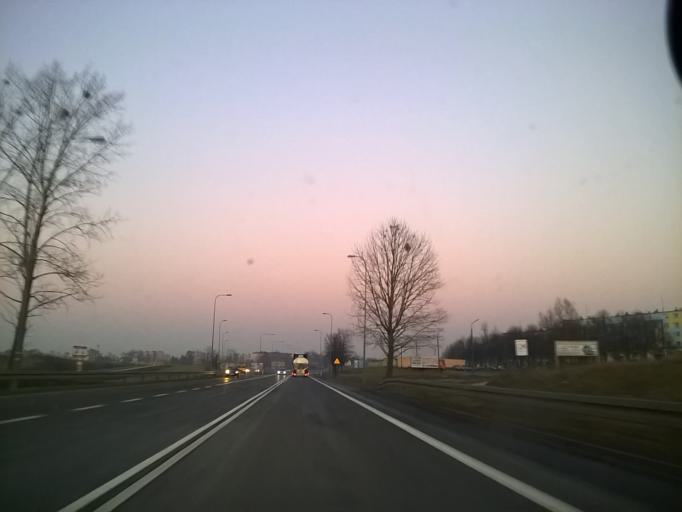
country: PL
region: Warmian-Masurian Voivodeship
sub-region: Powiat olsztynski
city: Barczewo
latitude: 53.8355
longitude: 20.6869
